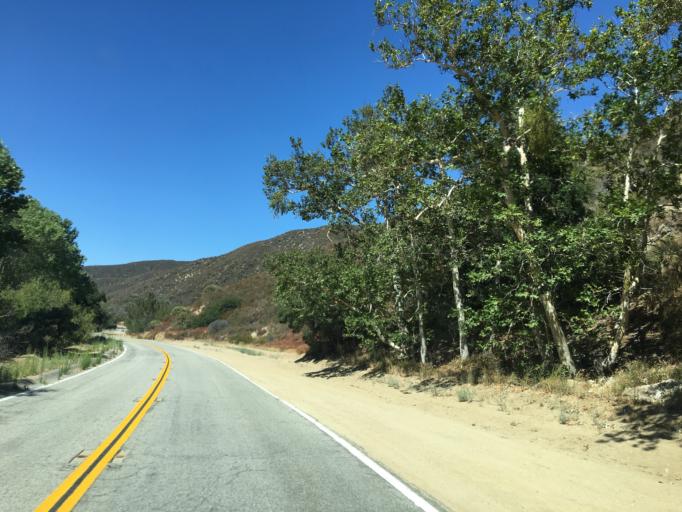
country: US
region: California
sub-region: Los Angeles County
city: Green Valley
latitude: 34.6446
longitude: -118.5183
